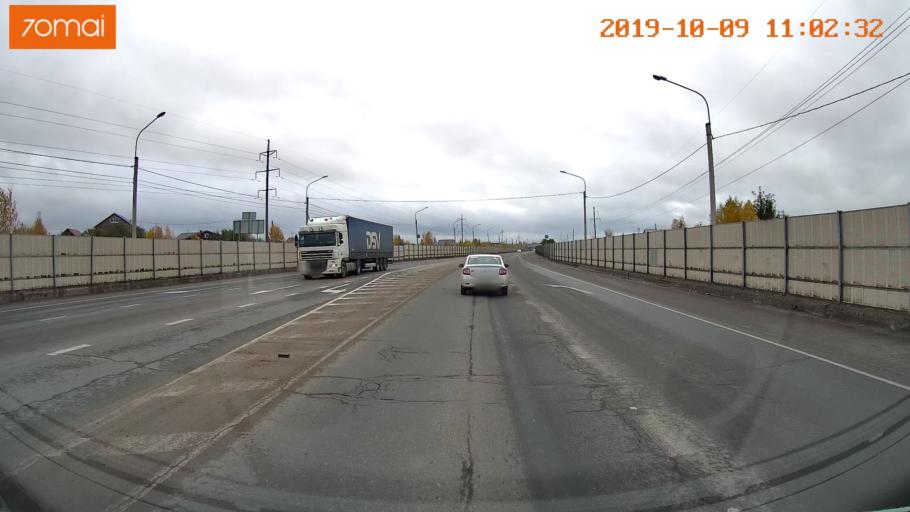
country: RU
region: Vologda
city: Vologda
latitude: 59.2314
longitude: 39.7745
